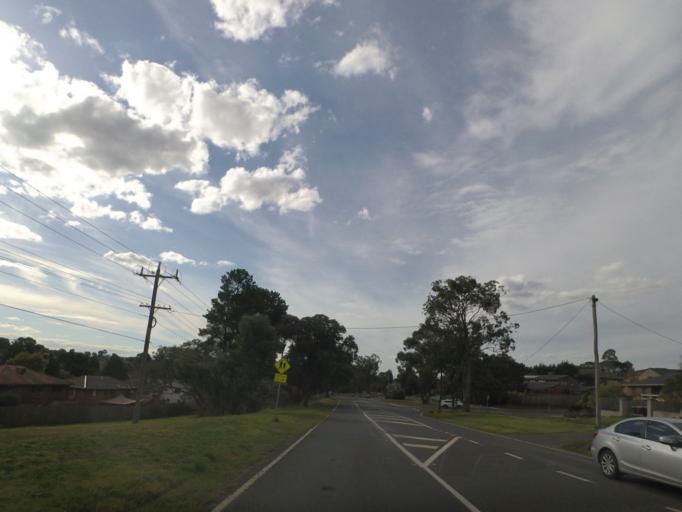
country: AU
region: Victoria
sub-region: Manningham
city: Donvale
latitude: -37.7601
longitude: 145.1738
